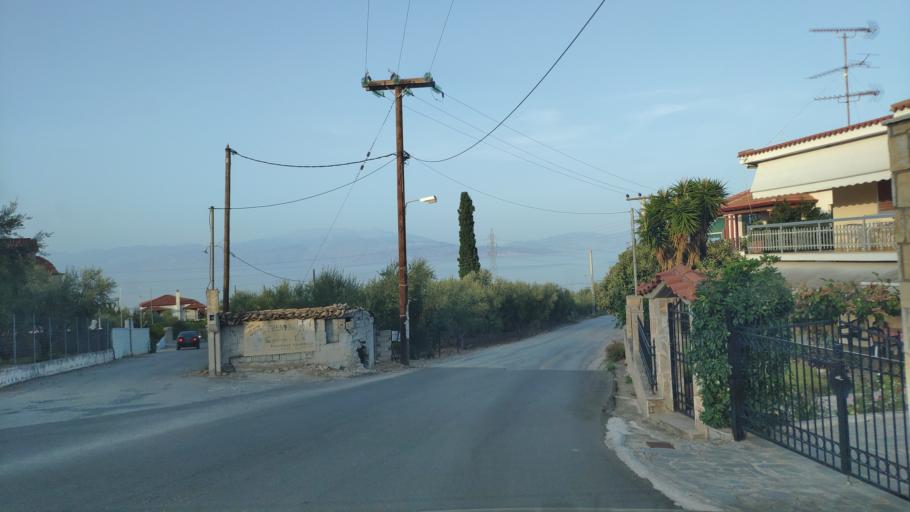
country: GR
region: West Greece
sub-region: Nomos Achaias
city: Aiyira
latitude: 38.1281
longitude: 22.4000
